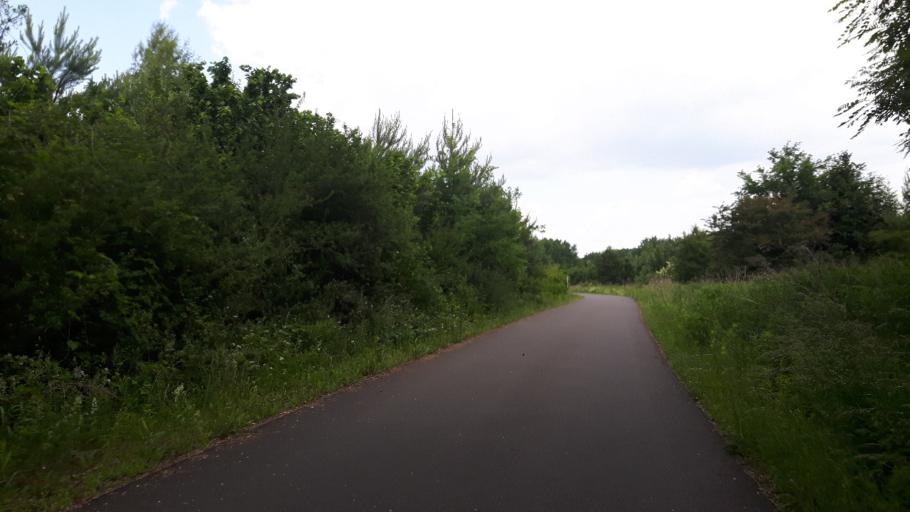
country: DE
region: Saxony-Anhalt
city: Grafenhainichen
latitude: 51.7079
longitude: 12.4640
